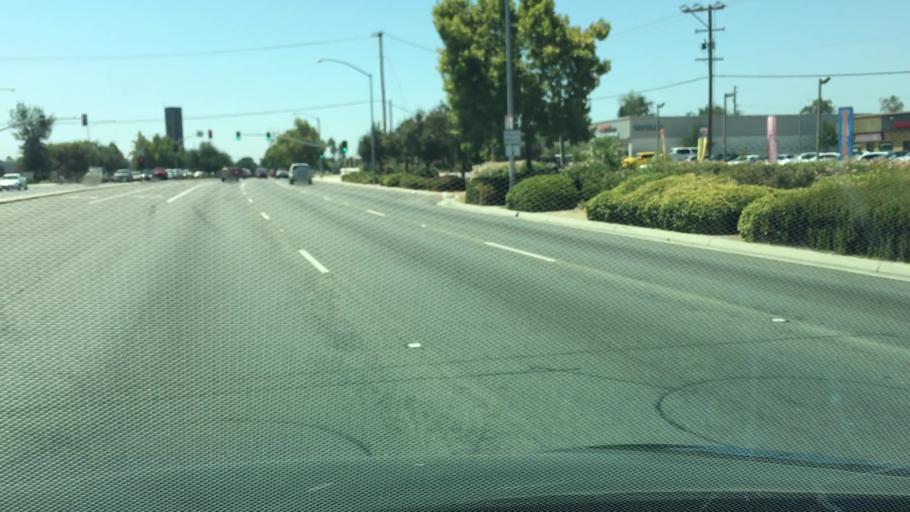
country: US
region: California
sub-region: Fresno County
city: Fresno
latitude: 36.8371
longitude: -119.7979
